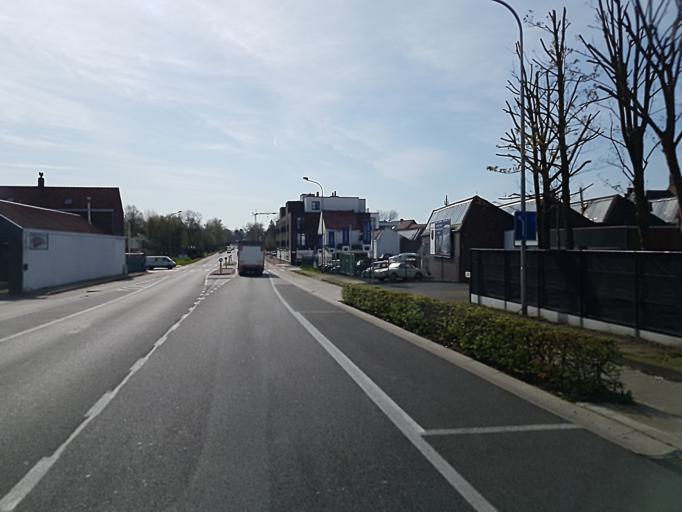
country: BE
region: Flanders
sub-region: Provincie West-Vlaanderen
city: Deerlijk
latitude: 50.8365
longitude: 3.4047
